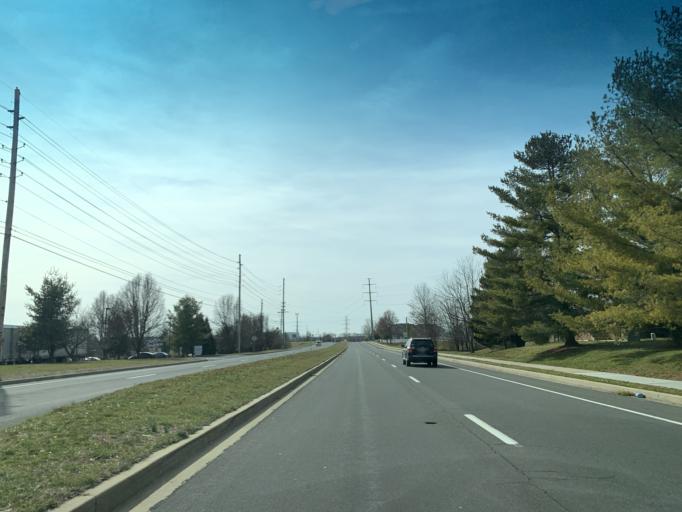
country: US
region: Maryland
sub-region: Frederick County
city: Ballenger Creek
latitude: 39.3676
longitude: -77.4312
